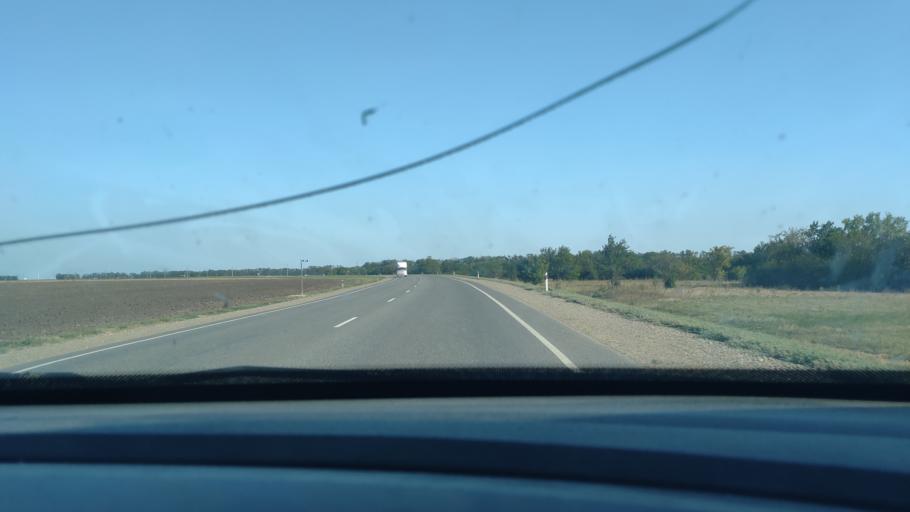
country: RU
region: Krasnodarskiy
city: Staroshcherbinovskaya
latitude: 46.6144
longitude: 38.6324
